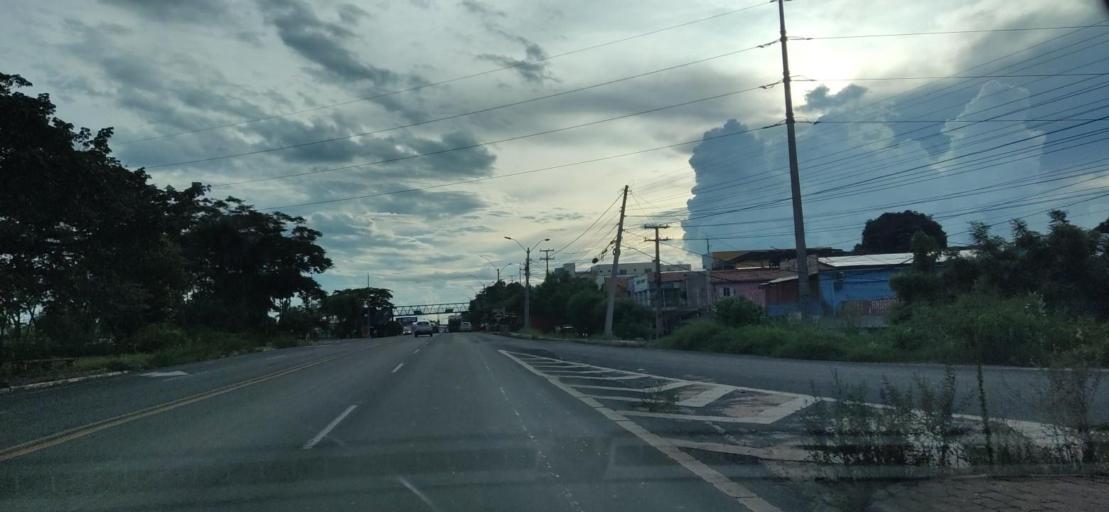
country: BR
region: Piaui
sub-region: Teresina
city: Teresina
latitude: -5.1174
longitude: -42.7838
